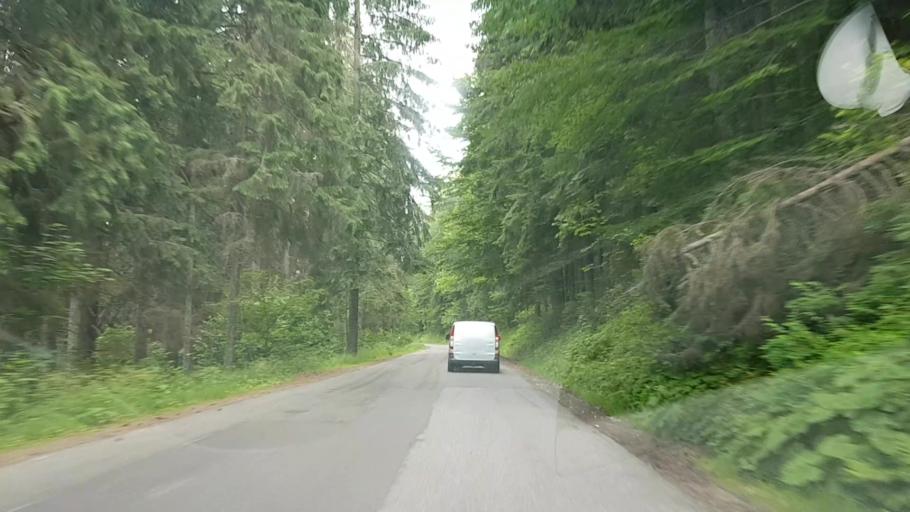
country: RO
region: Harghita
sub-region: Comuna Remetea
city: Remetea
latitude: 46.6737
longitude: 25.3392
